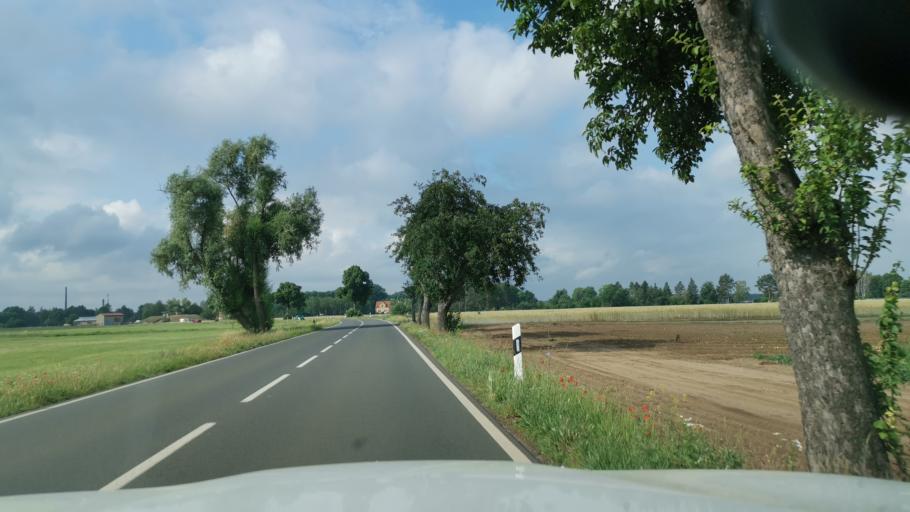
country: DE
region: Saxony-Anhalt
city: Annaburg
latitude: 51.7446
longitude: 13.0405
